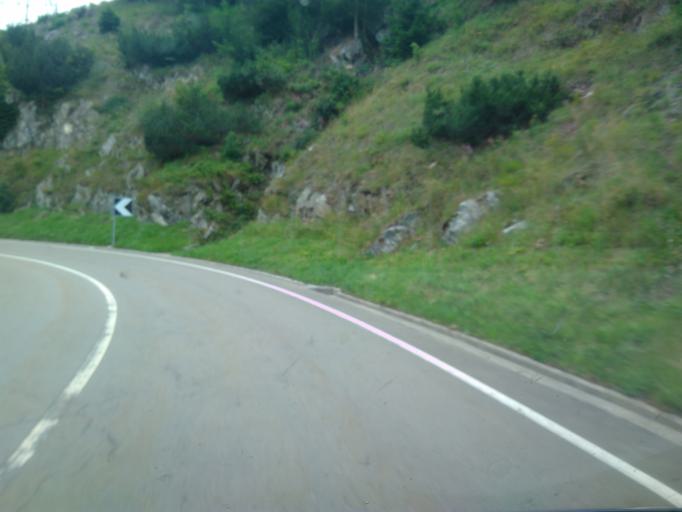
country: CH
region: Ticino
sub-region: Leventina District
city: Airolo
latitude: 46.5270
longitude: 8.5866
